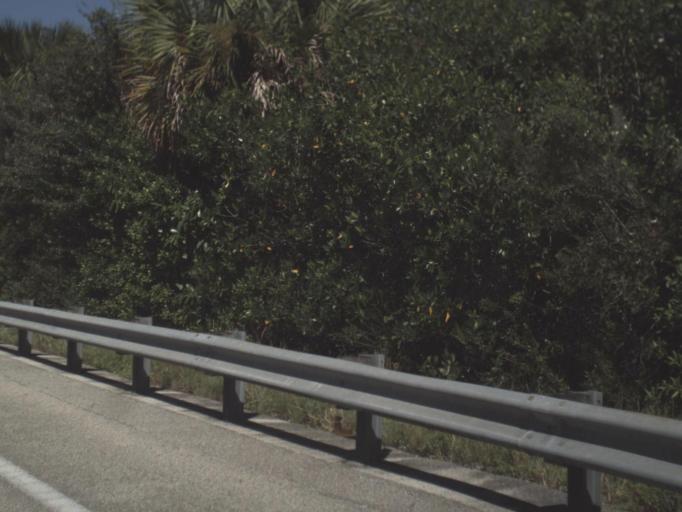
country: US
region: Florida
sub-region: Collier County
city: Marco
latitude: 25.9624
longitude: -81.5204
